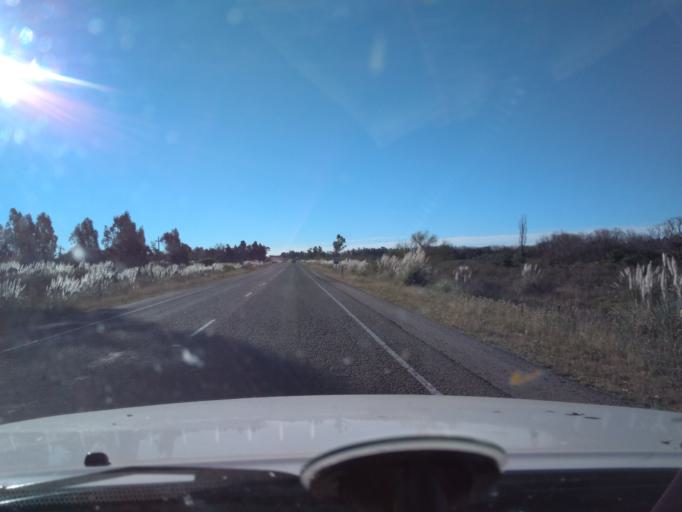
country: UY
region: Canelones
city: Sauce
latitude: -34.6016
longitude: -56.0498
